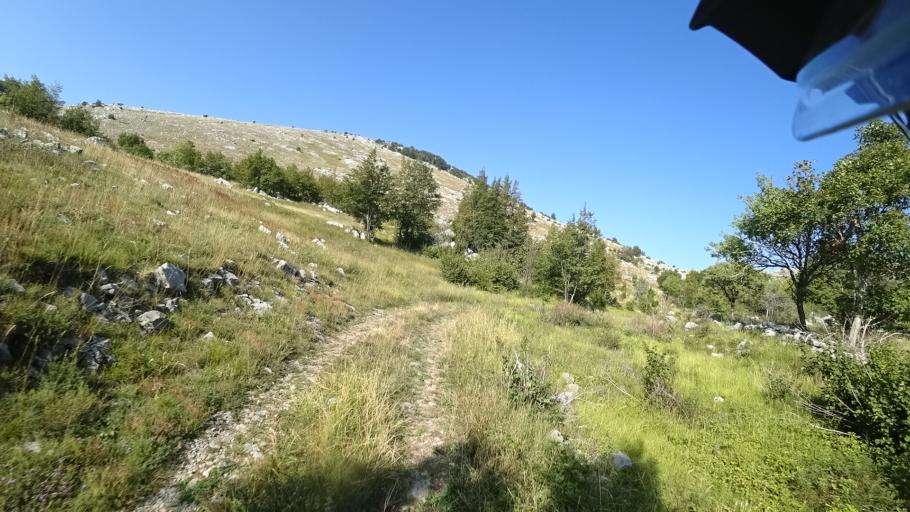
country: HR
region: Sibensko-Kniniska
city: Knin
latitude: 44.2003
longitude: 16.1590
